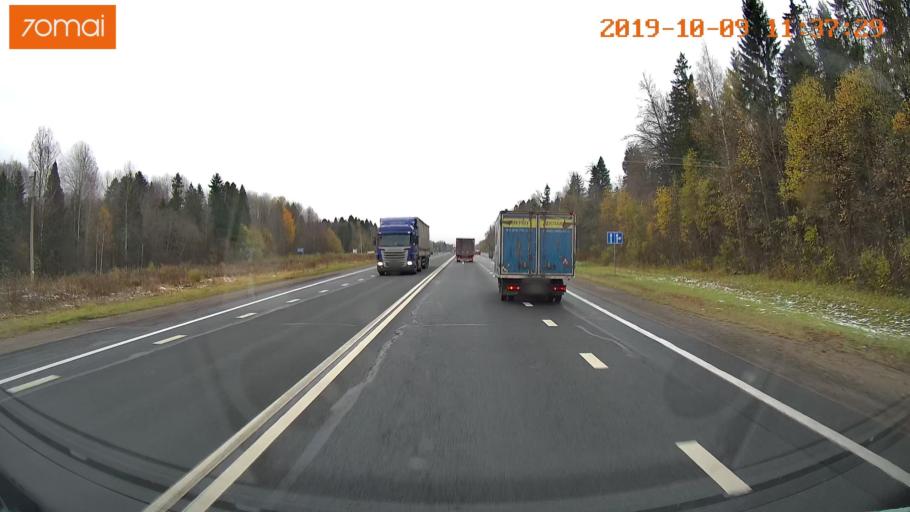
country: RU
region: Vologda
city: Gryazovets
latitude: 58.9789
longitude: 40.1467
